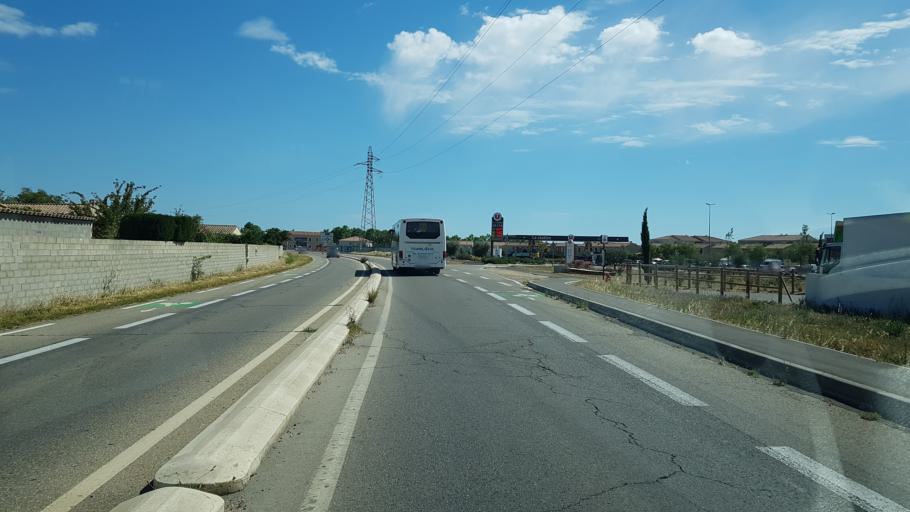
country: FR
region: Provence-Alpes-Cote d'Azur
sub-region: Departement des Bouches-du-Rhone
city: Saint-Martin-de-Crau
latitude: 43.6411
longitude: 4.7986
